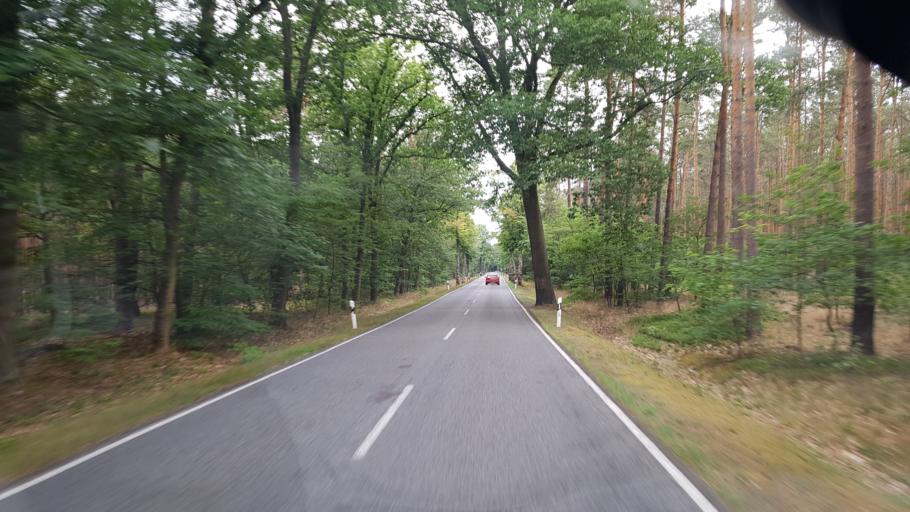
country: DE
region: Brandenburg
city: Dahme
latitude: 51.8373
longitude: 13.4140
